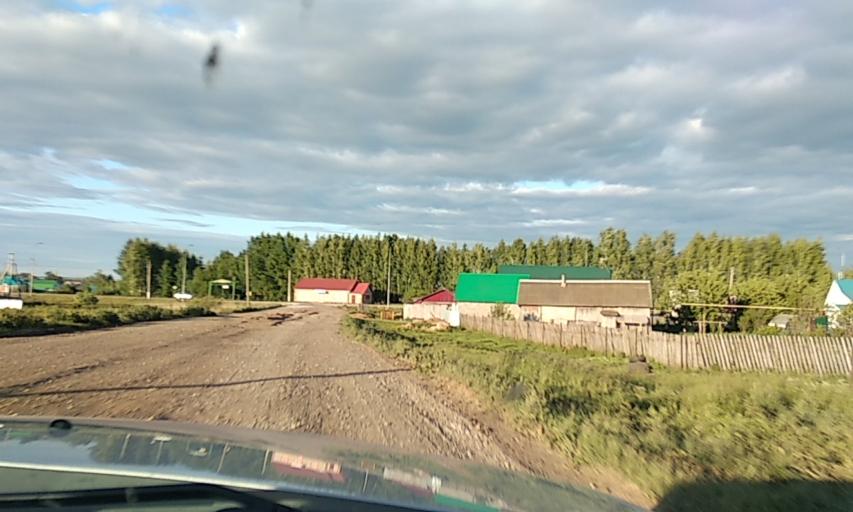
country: RU
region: Tatarstan
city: Nurlat
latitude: 54.8414
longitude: 50.7877
